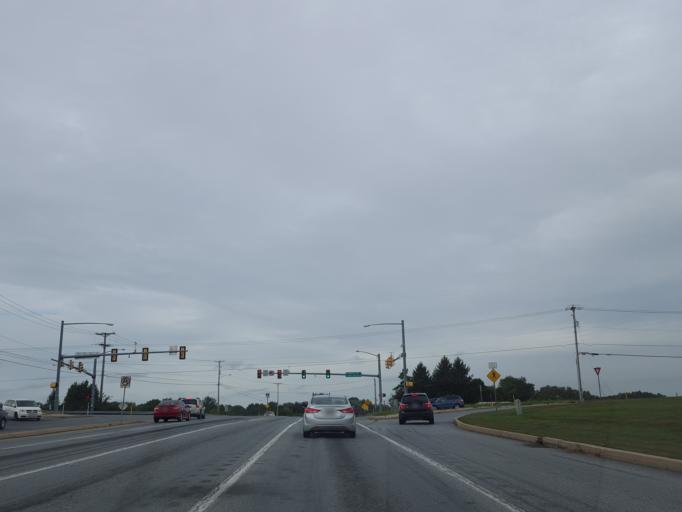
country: US
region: Pennsylvania
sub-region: York County
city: Weigelstown
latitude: 39.9287
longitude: -76.8222
